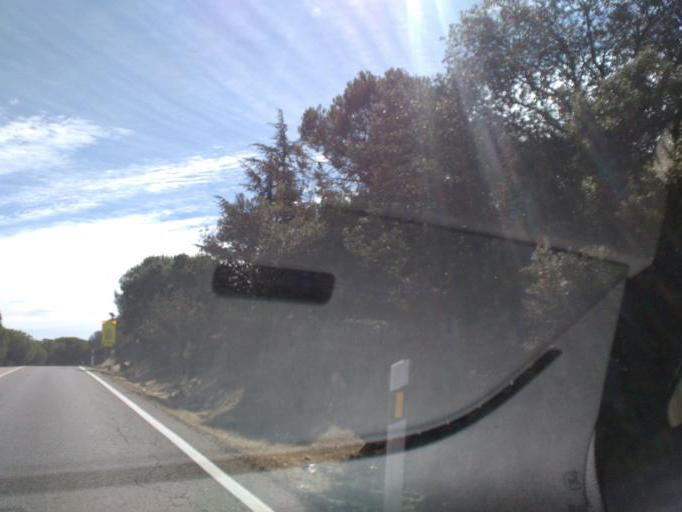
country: ES
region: Madrid
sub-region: Provincia de Madrid
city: Galapagar
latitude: 40.5640
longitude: -3.9720
